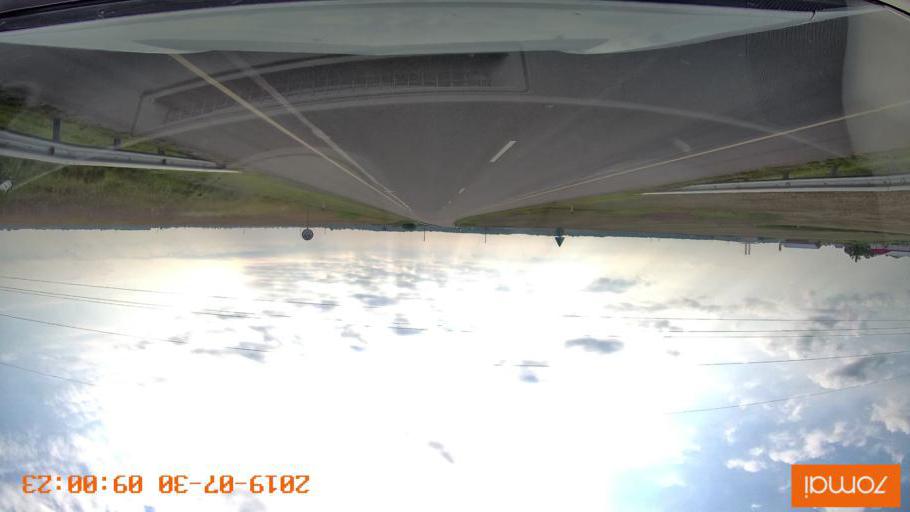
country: RU
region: Kaliningrad
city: Gusev
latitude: 54.6148
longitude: 22.1801
